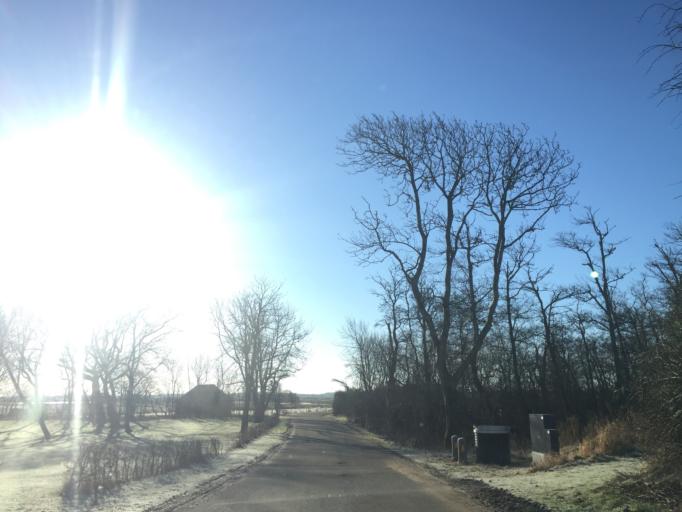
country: DK
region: Central Jutland
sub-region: Holstebro Kommune
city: Vinderup
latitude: 56.5642
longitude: 8.7624
